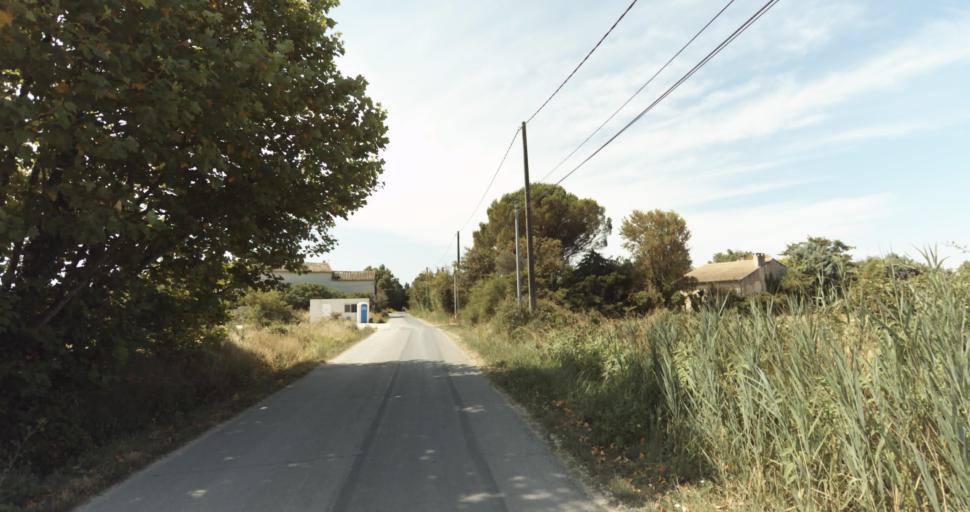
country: FR
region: Provence-Alpes-Cote d'Azur
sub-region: Departement du Vaucluse
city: Monteux
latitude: 44.0253
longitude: 4.9933
